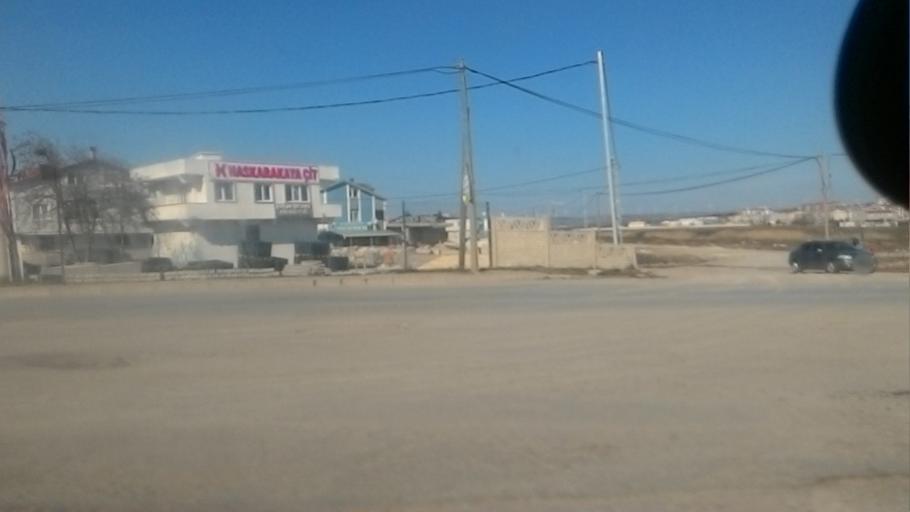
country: TR
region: Istanbul
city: Silivri
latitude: 41.0805
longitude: 28.2318
